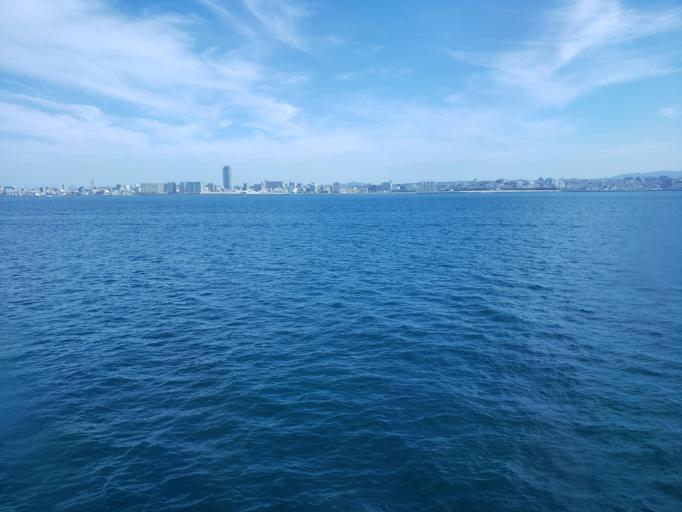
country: JP
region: Hyogo
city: Akashi
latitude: 34.6254
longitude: 134.9991
